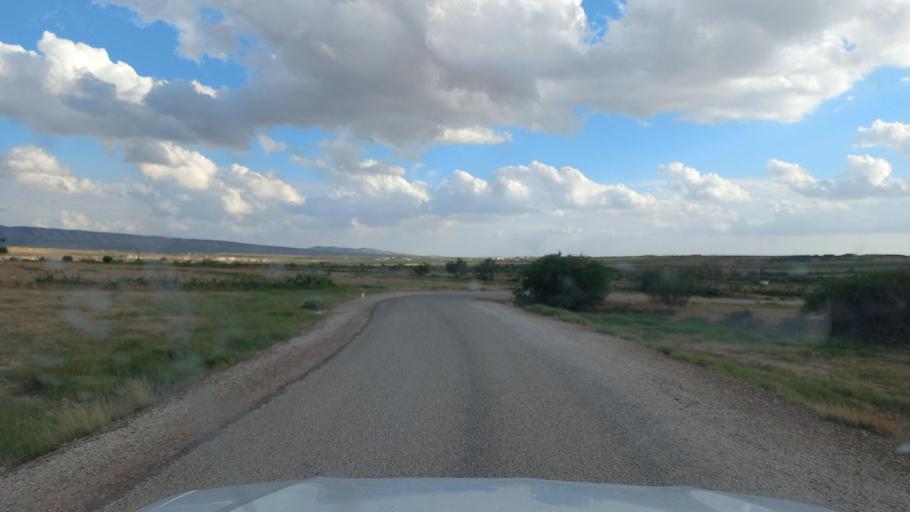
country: TN
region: Al Qasrayn
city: Sbiba
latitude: 35.3767
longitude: 9.0723
